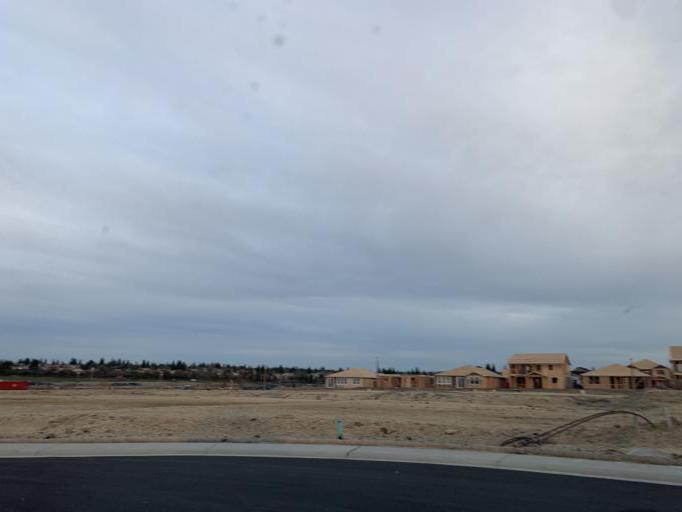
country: US
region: California
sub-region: Placer County
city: Lincoln
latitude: 38.8614
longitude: -121.2901
